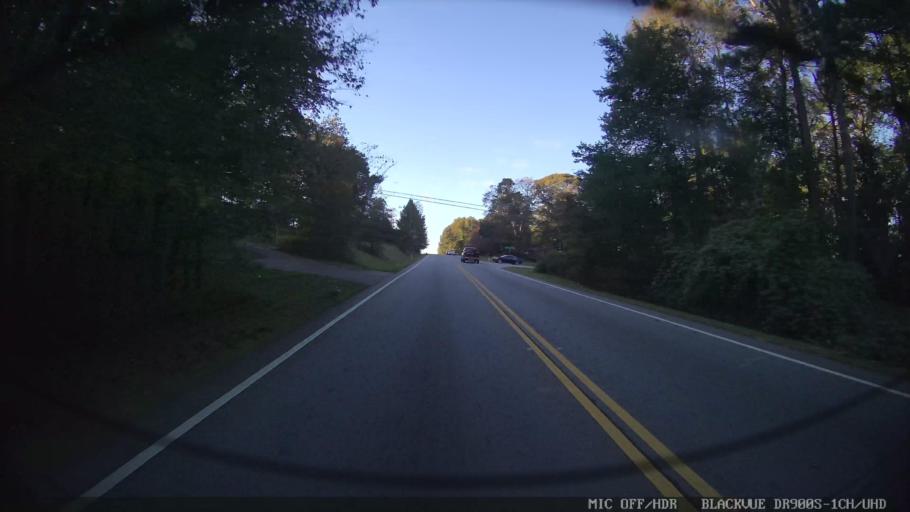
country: US
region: Georgia
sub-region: Clayton County
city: Lake City
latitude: 33.5942
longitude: -84.2952
